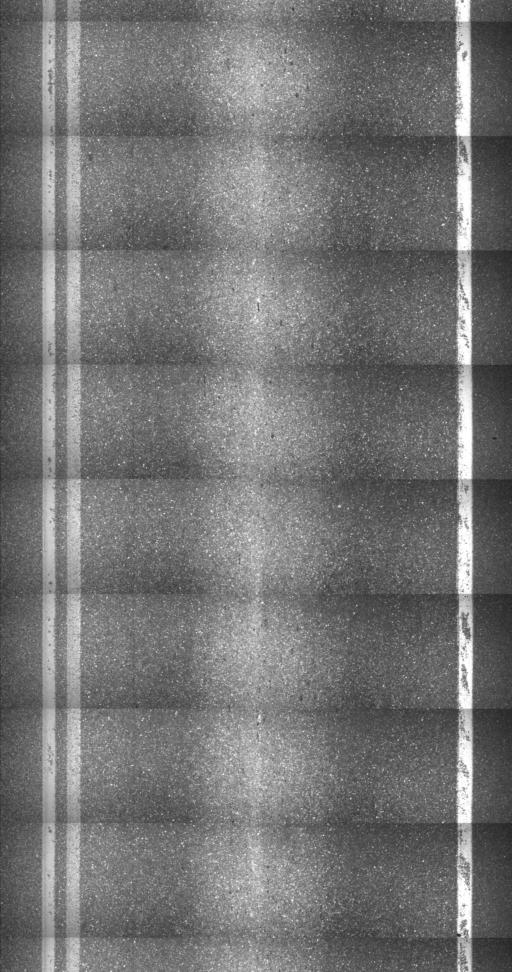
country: US
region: Vermont
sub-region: Franklin County
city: Saint Albans
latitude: 44.8119
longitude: -73.0649
